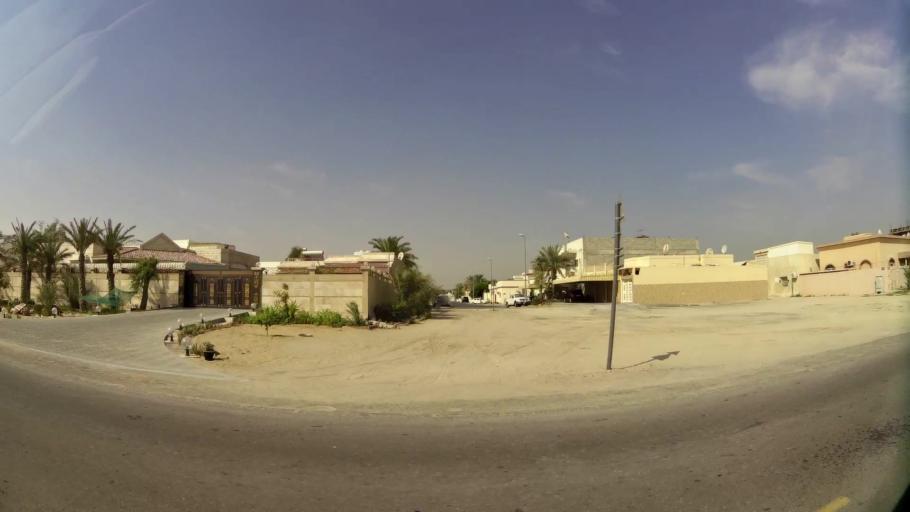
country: AE
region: Ash Shariqah
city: Sharjah
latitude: 25.2638
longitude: 55.3966
